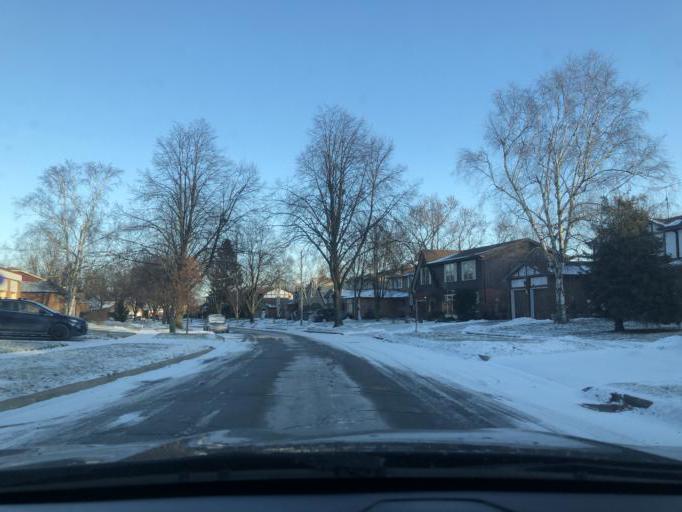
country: CA
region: Ontario
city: Scarborough
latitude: 43.7834
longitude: -79.1539
